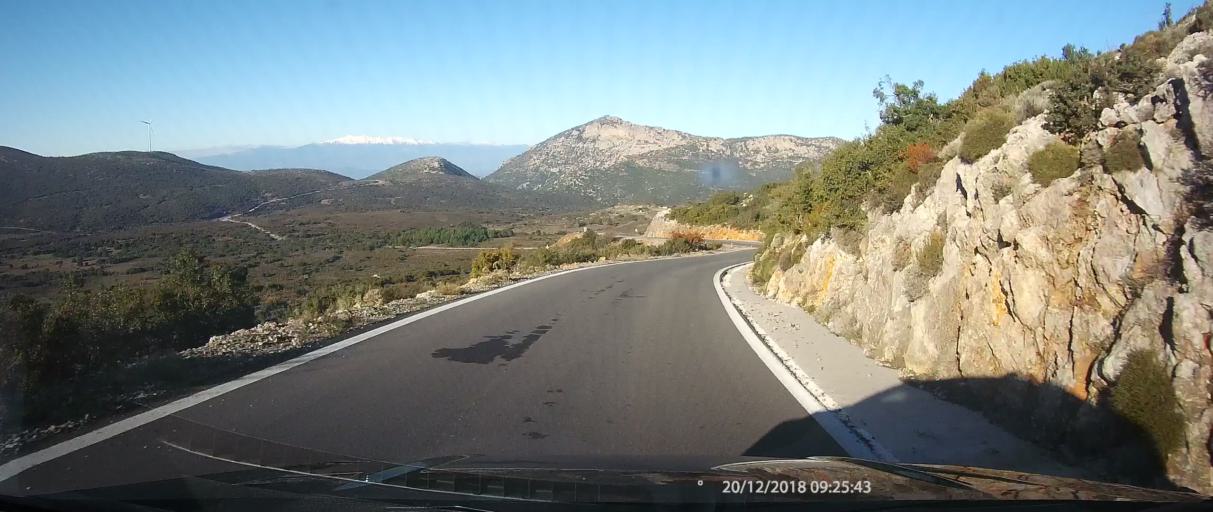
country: GR
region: Peloponnese
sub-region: Nomos Lakonias
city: Molaoi
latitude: 36.9609
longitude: 22.8820
